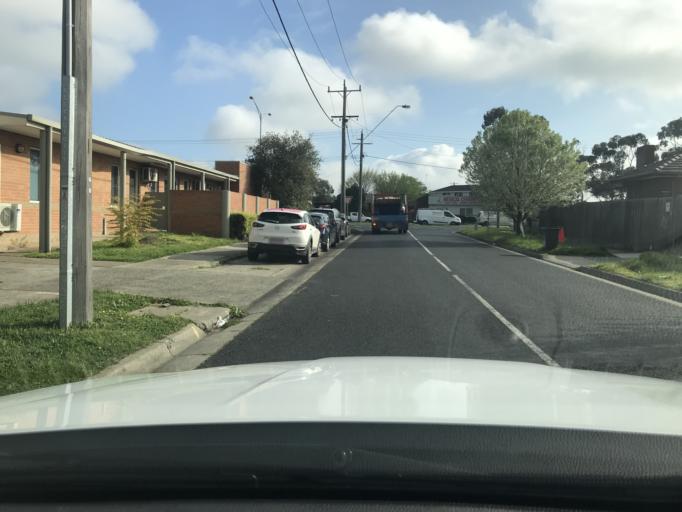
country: AU
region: Victoria
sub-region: Hume
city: Craigieburn
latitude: -37.5991
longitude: 144.9372
